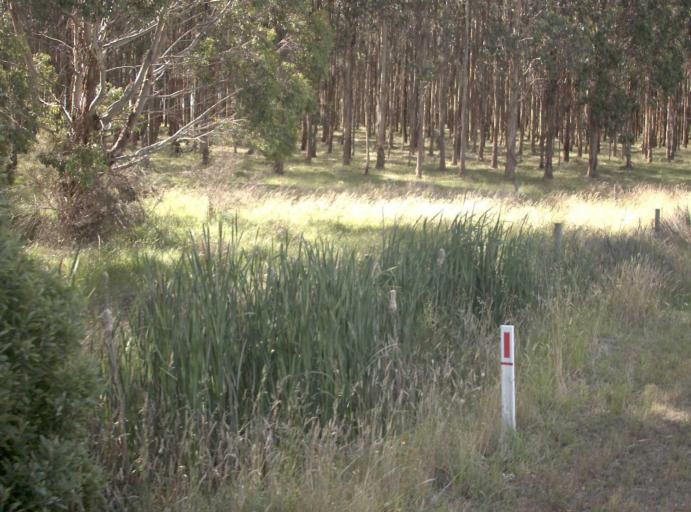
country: AU
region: Victoria
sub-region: Latrobe
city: Morwell
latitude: -38.2144
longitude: 146.3989
